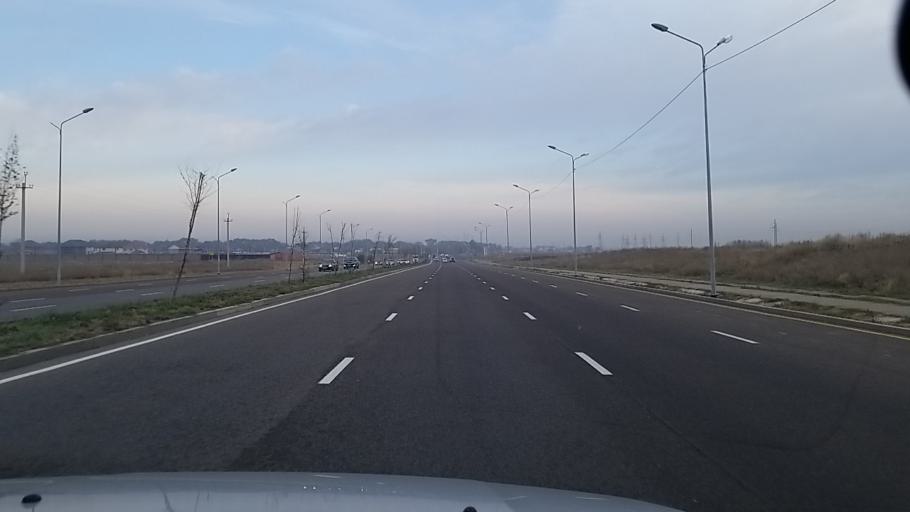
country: KZ
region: Almaty Oblysy
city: Burunday
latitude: 43.3450
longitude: 76.8339
